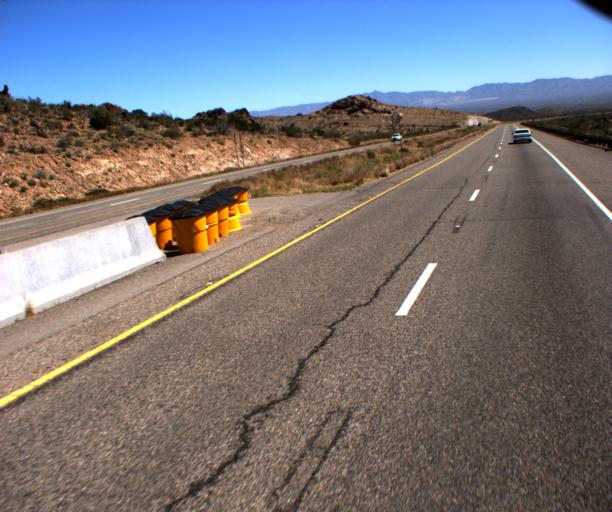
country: US
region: Arizona
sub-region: Mohave County
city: Golden Valley
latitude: 35.2257
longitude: -114.3804
